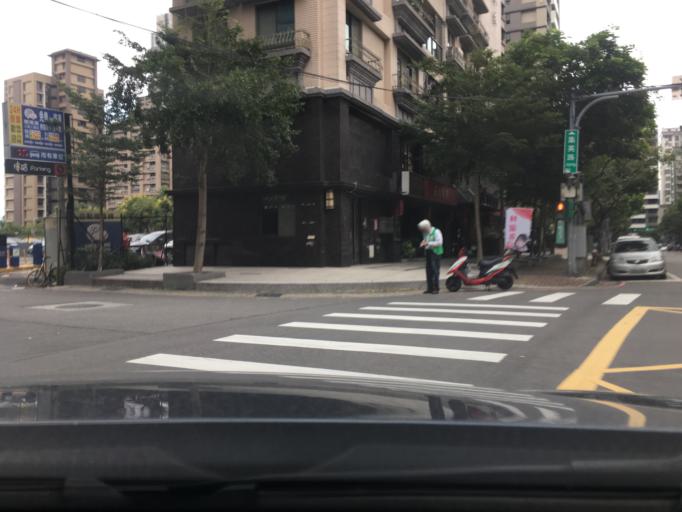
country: TW
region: Taipei
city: Taipei
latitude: 25.0868
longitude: 121.4857
